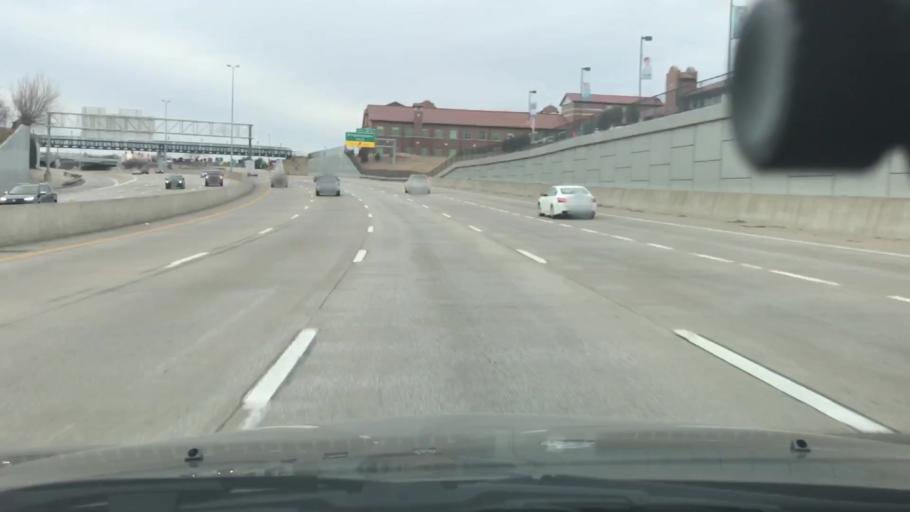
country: US
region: Missouri
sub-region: Saint Louis County
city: University City
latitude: 38.6322
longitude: -90.2608
